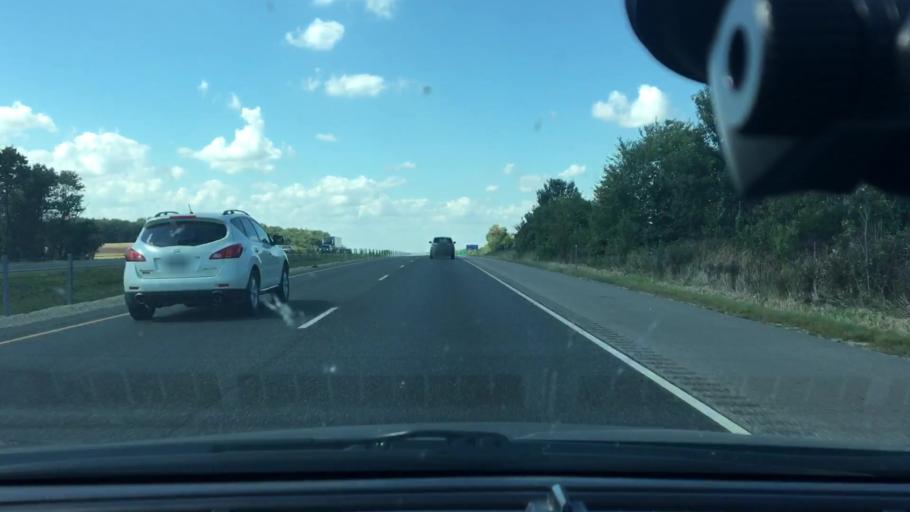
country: US
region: Wisconsin
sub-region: Saint Croix County
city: Hammond
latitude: 44.9418
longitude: -92.4185
